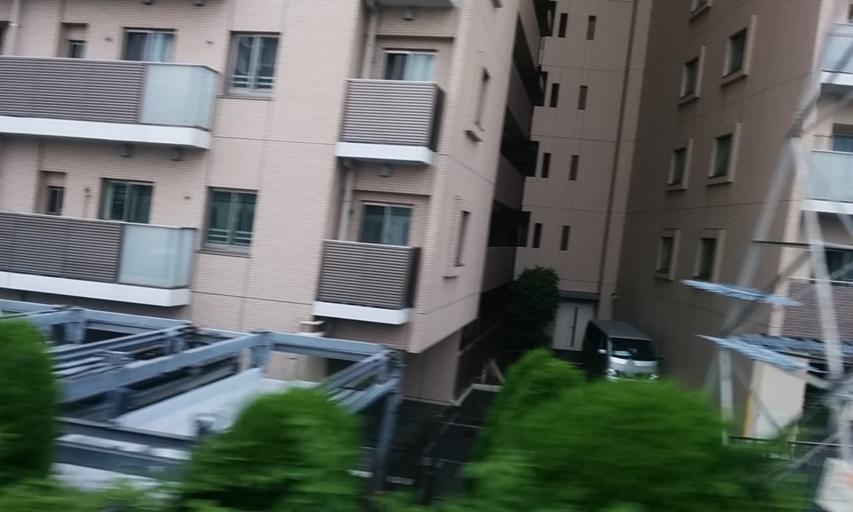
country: JP
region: Chiba
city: Matsudo
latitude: 35.7688
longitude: 139.8646
